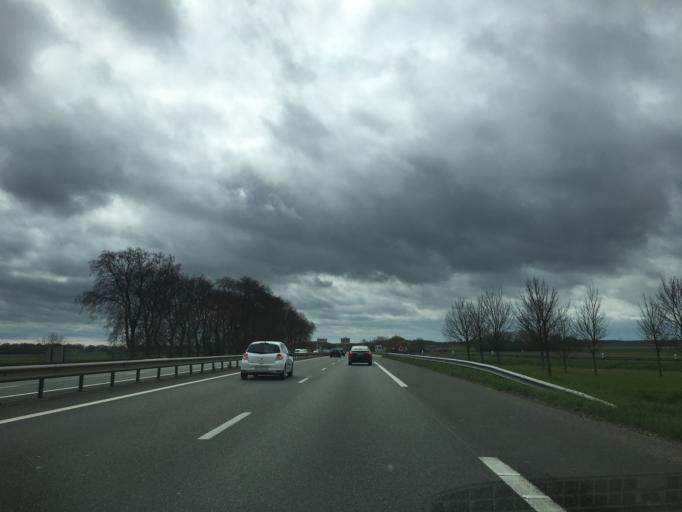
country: FR
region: Ile-de-France
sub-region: Departement de Seine-et-Marne
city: Moissy-Cramayel
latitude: 48.6312
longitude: 2.6288
